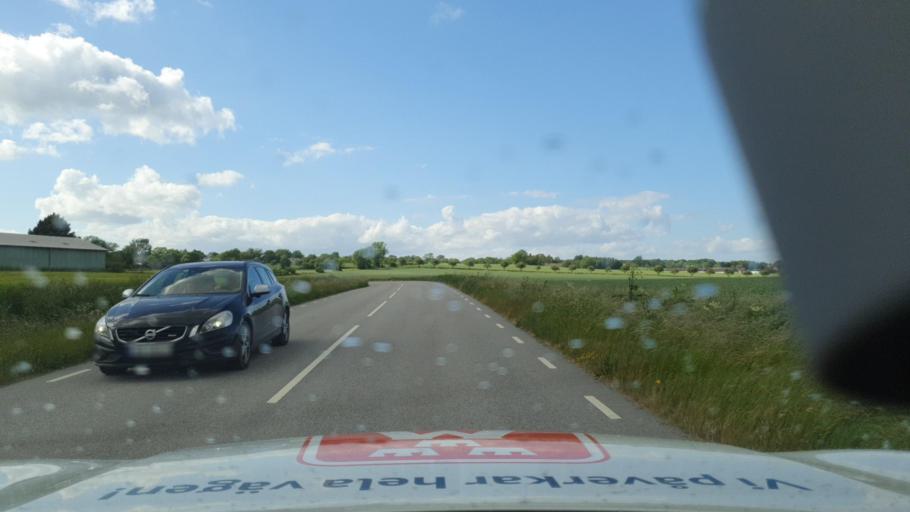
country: SE
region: Skane
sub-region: Simrishamns Kommun
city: Simrishamn
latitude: 55.5510
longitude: 14.3230
